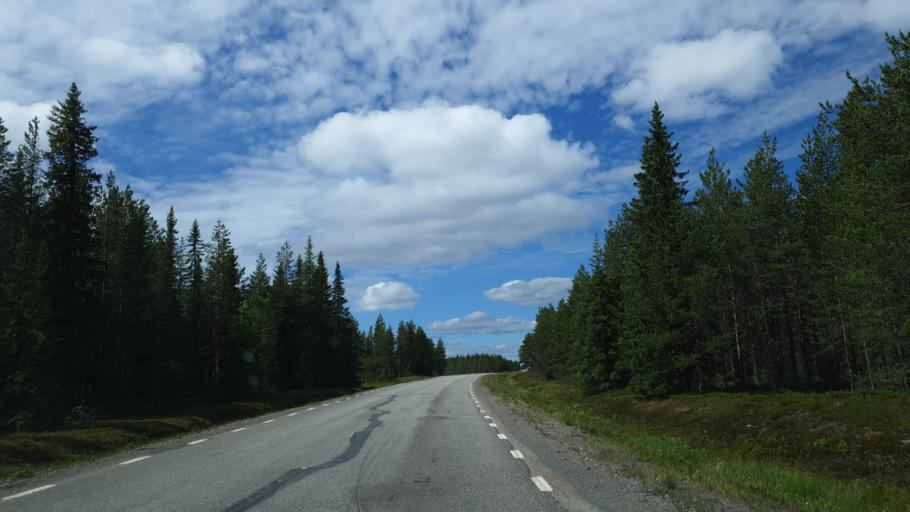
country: SE
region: Vaesterbotten
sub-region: Mala Kommun
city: Mala
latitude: 65.5643
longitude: 18.2851
